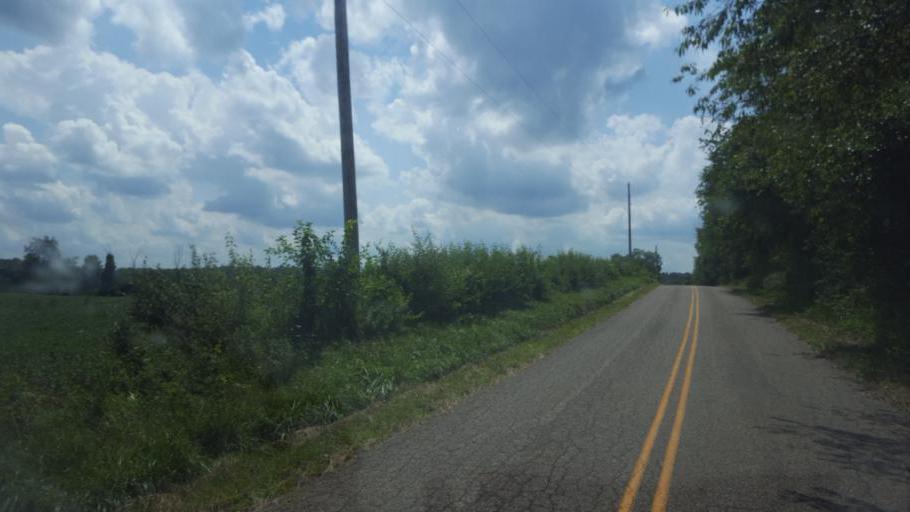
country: US
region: Ohio
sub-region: Knox County
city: Mount Vernon
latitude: 40.3928
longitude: -82.5795
